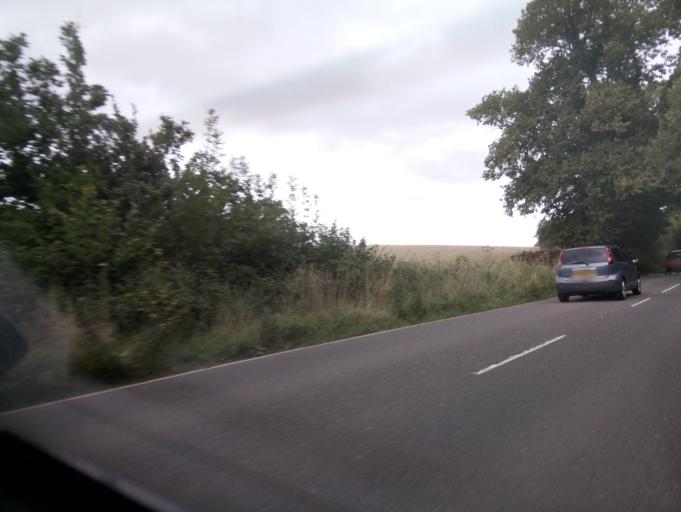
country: GB
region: England
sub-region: Devon
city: Exminster
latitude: 50.6655
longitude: -3.4825
